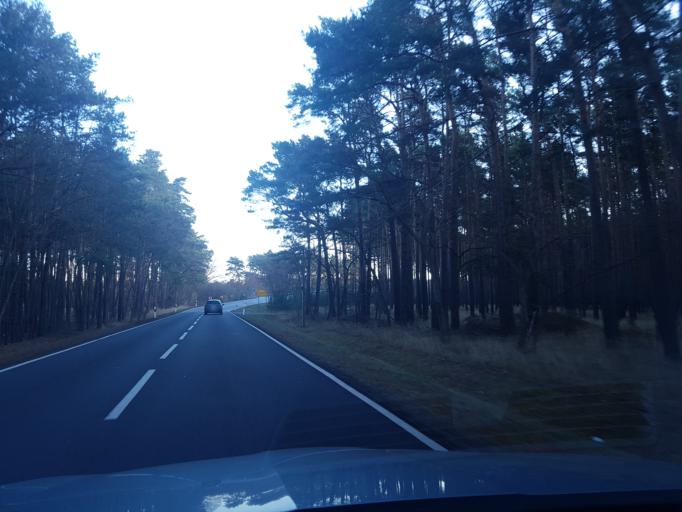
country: DE
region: Brandenburg
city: Halbe
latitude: 52.0251
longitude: 13.7196
